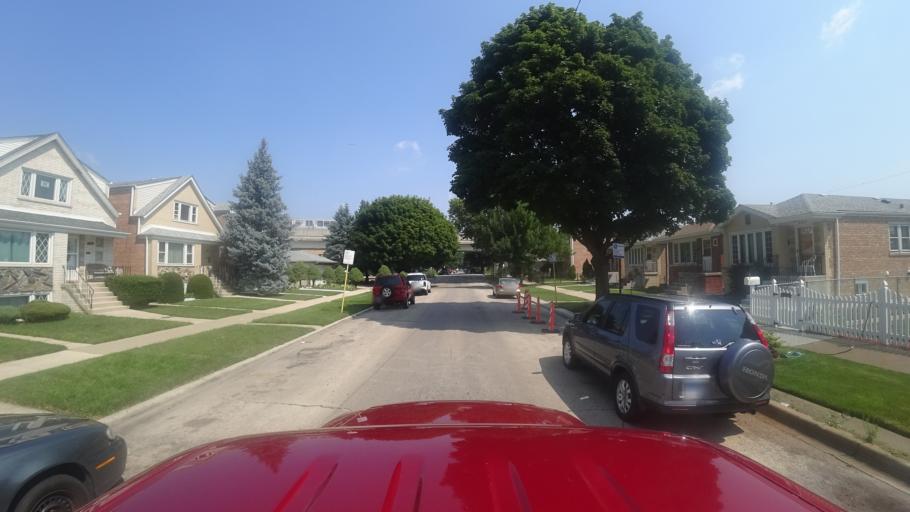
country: US
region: Illinois
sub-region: Cook County
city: Cicero
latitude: 41.7972
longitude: -87.7294
